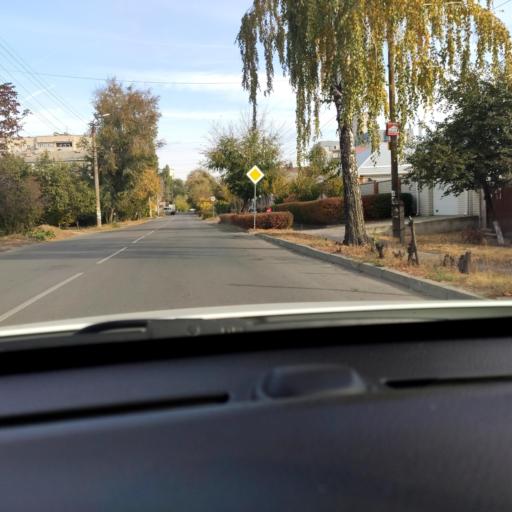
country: RU
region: Voronezj
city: Voronezh
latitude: 51.6437
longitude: 39.1722
